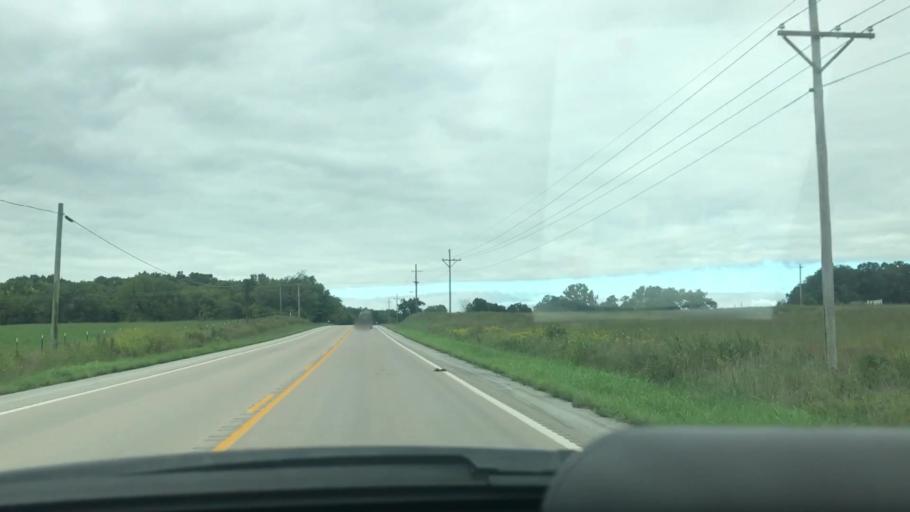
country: US
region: Missouri
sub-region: Hickory County
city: Hermitage
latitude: 37.8663
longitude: -93.1792
